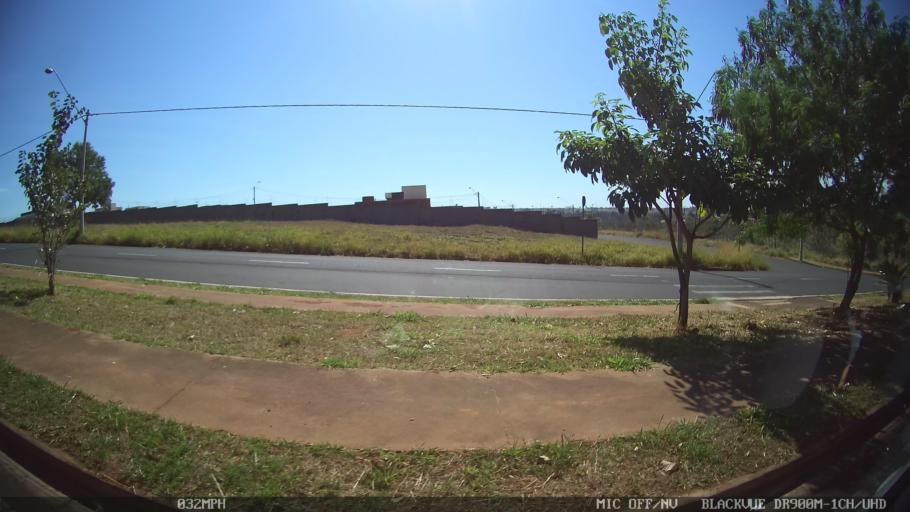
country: BR
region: Sao Paulo
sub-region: Sao Jose Do Rio Preto
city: Sao Jose do Rio Preto
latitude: -20.7666
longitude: -49.4174
